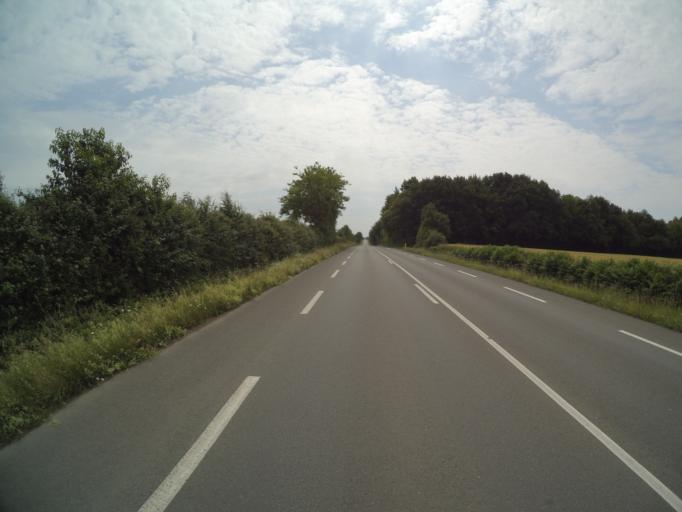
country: FR
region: Pays de la Loire
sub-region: Departement de la Vendee
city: Chavagnes-en-Paillers
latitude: 46.8863
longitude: -1.2159
